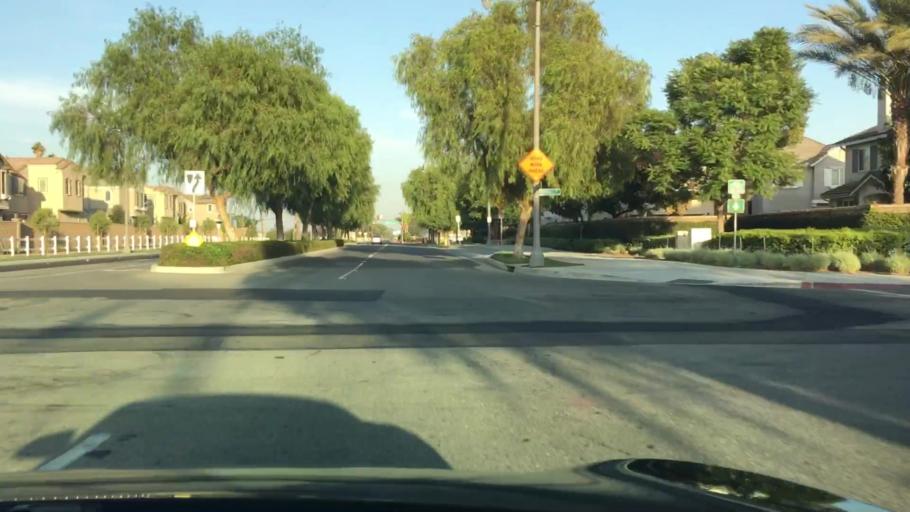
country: US
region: California
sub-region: San Bernardino County
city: Chino
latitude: 33.9902
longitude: -117.6530
